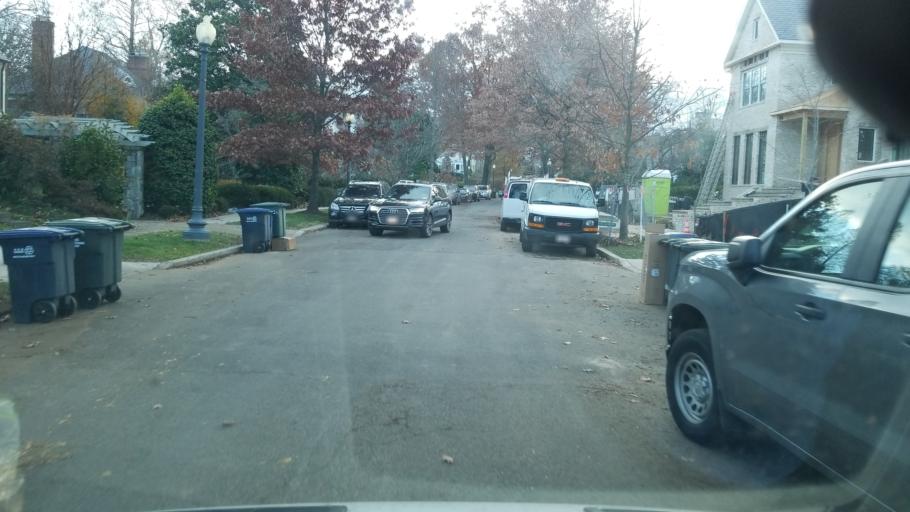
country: US
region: Maryland
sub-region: Montgomery County
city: Brookmont
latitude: 38.9384
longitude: -77.0962
